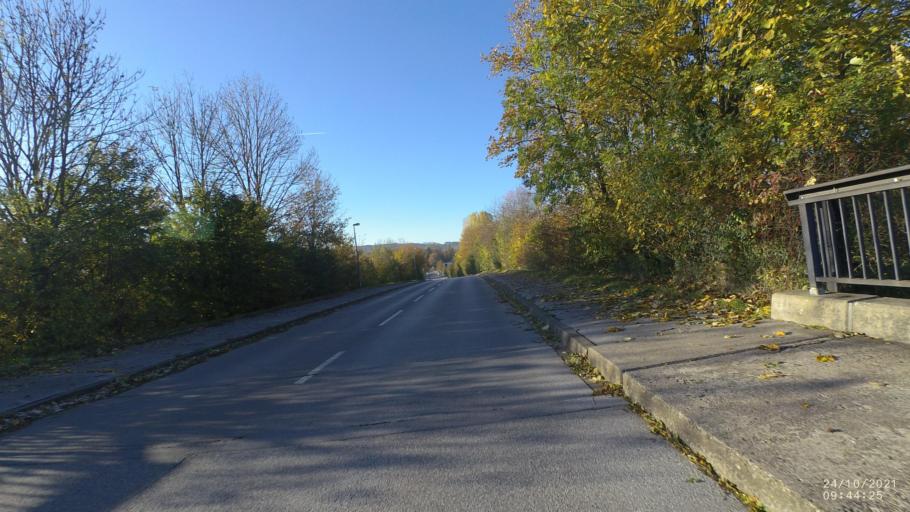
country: DE
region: North Rhine-Westphalia
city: Hemer
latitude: 51.3867
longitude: 7.8093
